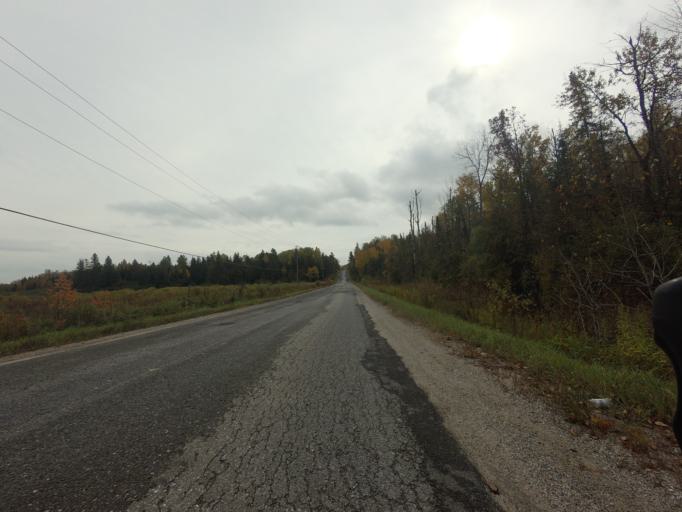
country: CA
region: Ontario
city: Perth
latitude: 45.1193
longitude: -76.5173
